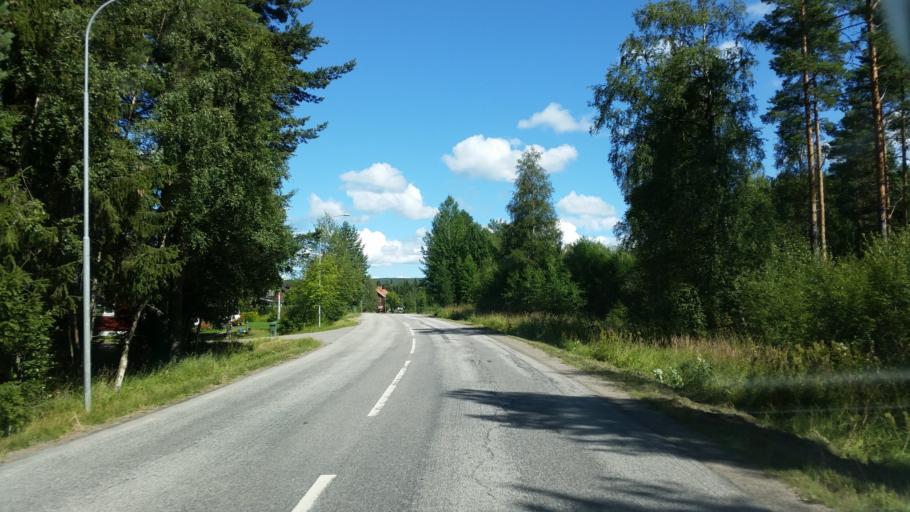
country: SE
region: Gaevleborg
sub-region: Ljusdals Kommun
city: Ljusdal
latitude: 61.8366
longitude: 16.1075
